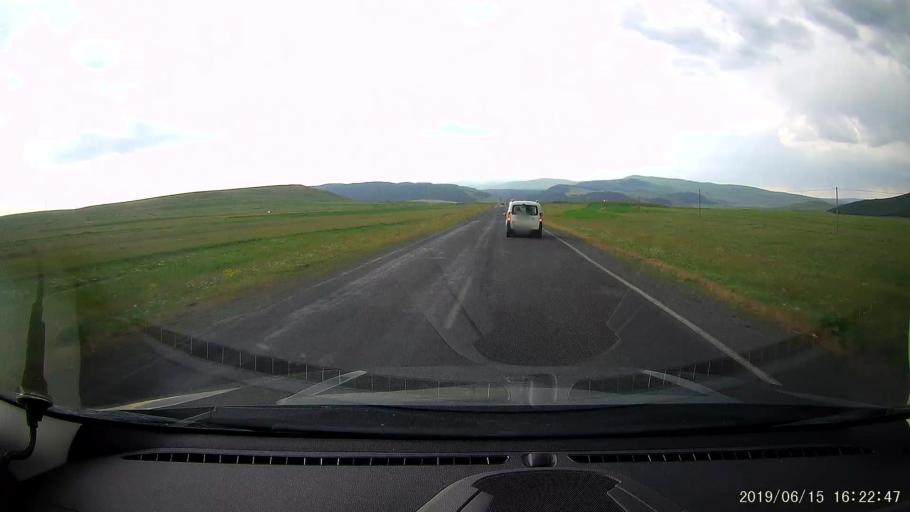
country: TR
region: Ardahan
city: Hanak
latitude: 41.1847
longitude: 42.8546
